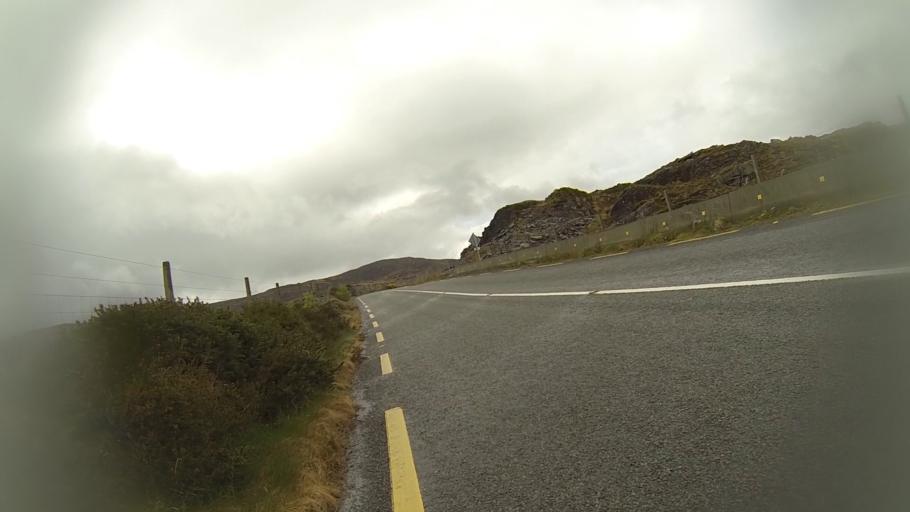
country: IE
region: Munster
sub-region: Ciarrai
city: Kenmare
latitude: 51.8002
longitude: -9.5772
